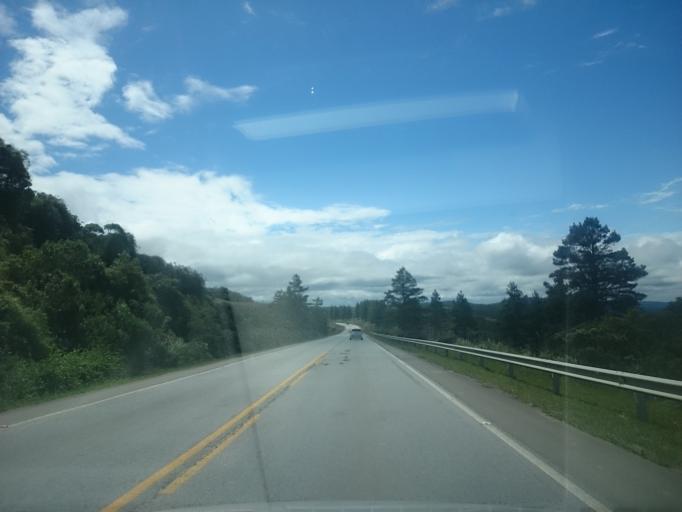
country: BR
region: Santa Catarina
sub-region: Anitapolis
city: Anitapolis
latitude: -27.6854
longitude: -49.1439
